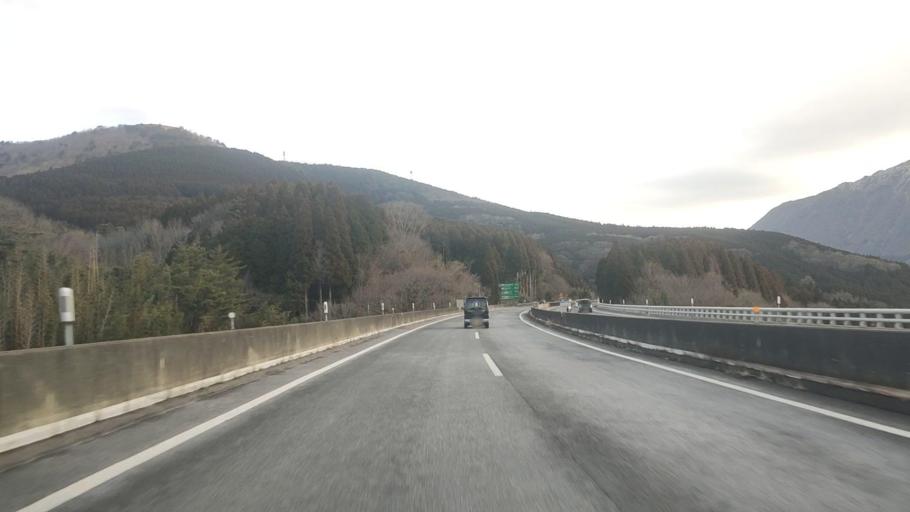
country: JP
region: Oita
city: Beppu
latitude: 33.2626
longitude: 131.3328
